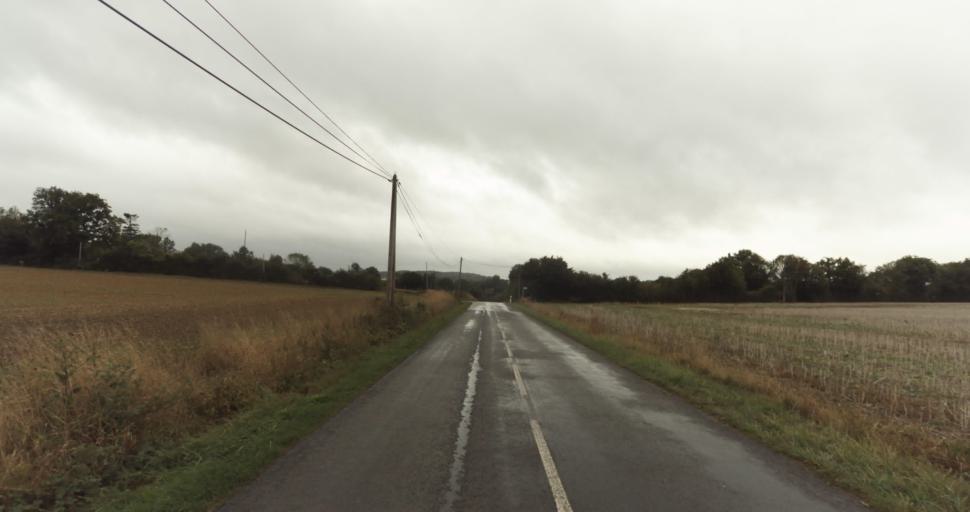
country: FR
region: Lower Normandy
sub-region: Departement de l'Orne
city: Sainte-Gauburge-Sainte-Colombe
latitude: 48.7289
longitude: 0.4339
